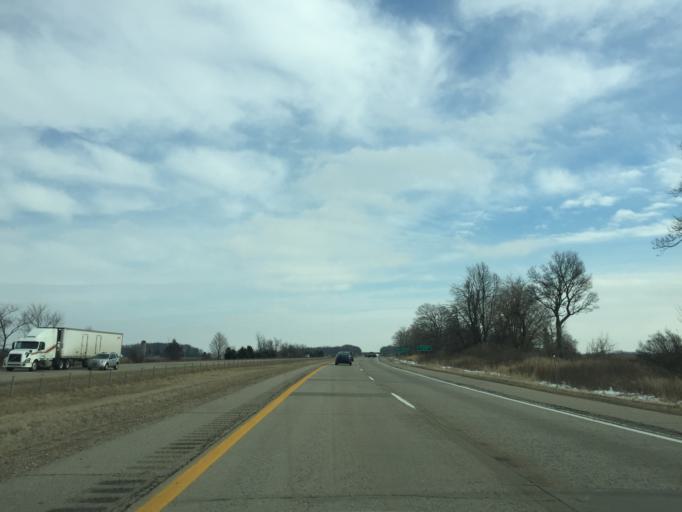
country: US
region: Michigan
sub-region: Ionia County
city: Saranac
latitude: 42.8791
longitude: -85.1451
